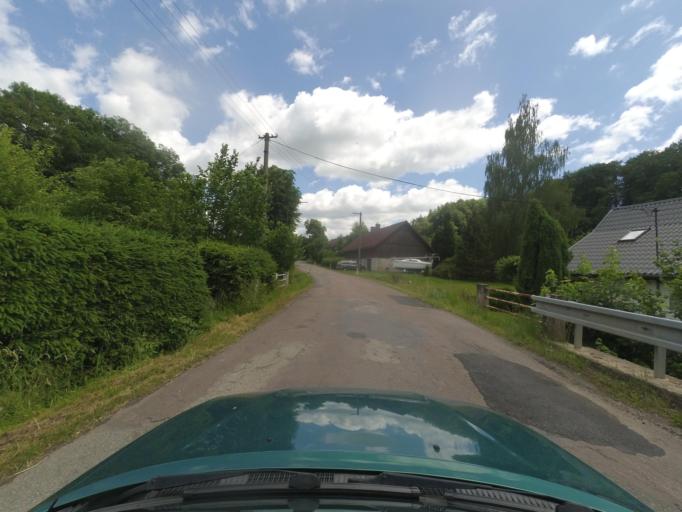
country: CZ
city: Rokytnice v Orlickych Horach
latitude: 50.1306
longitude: 16.4081
